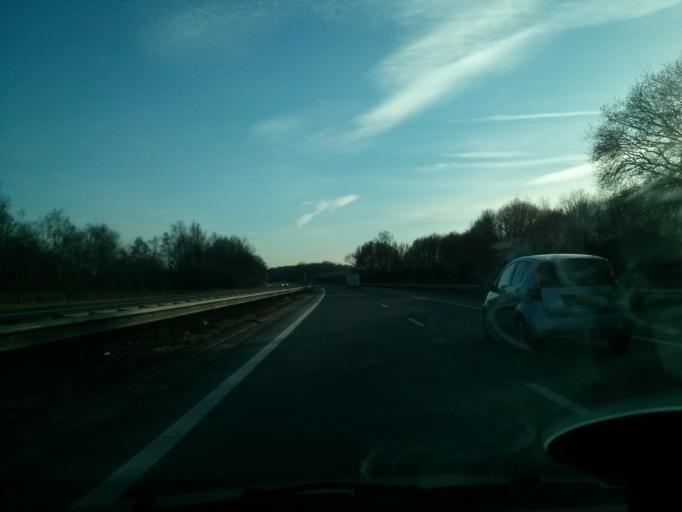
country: NL
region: Gelderland
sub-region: Gemeente Wijchen
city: Bergharen
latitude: 51.8336
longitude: 5.6856
